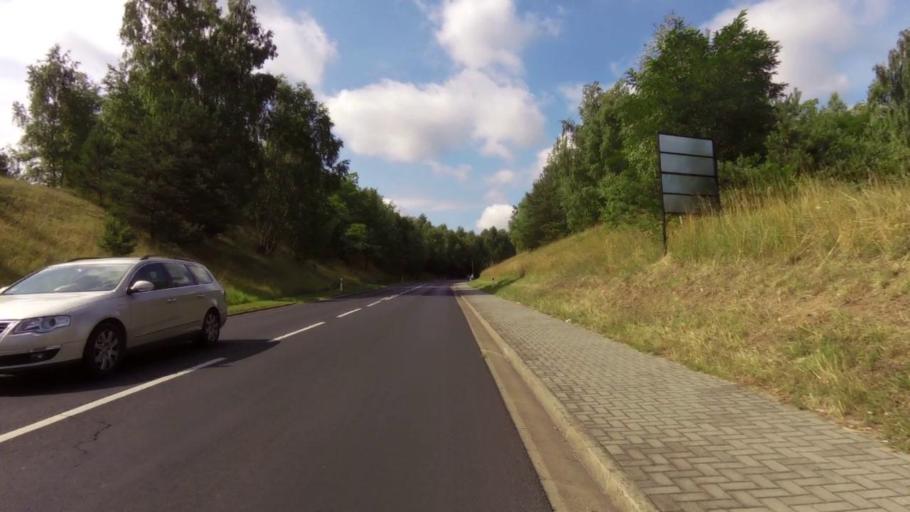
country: PL
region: West Pomeranian Voivodeship
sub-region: Powiat gryfinski
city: Cedynia
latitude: 52.8464
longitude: 14.1389
